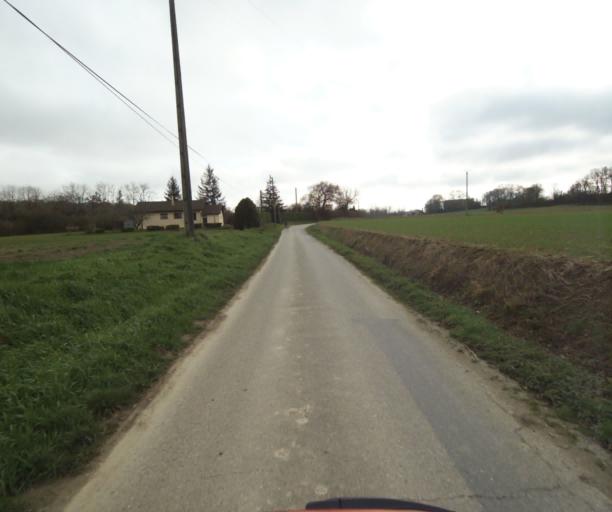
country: FR
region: Languedoc-Roussillon
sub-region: Departement de l'Aude
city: Belpech
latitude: 43.1808
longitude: 1.7342
